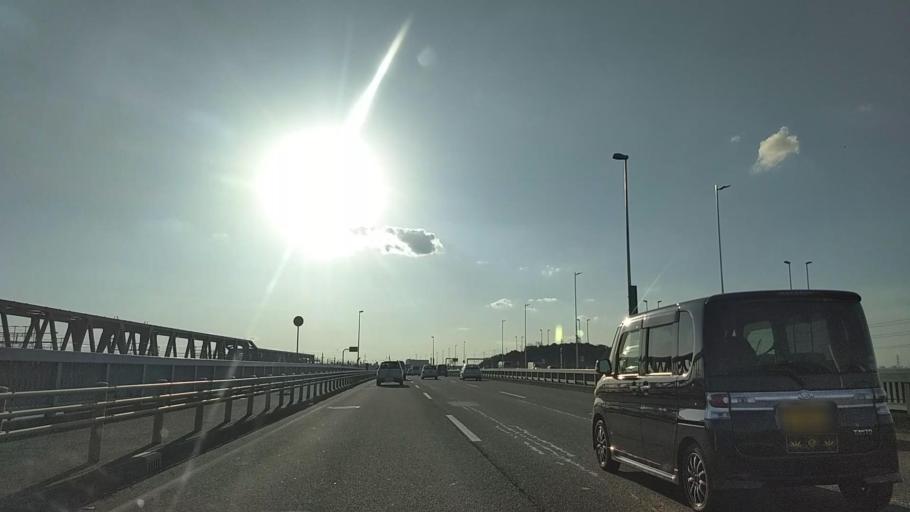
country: JP
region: Chiba
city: Funabashi
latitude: 35.6841
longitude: 139.9431
